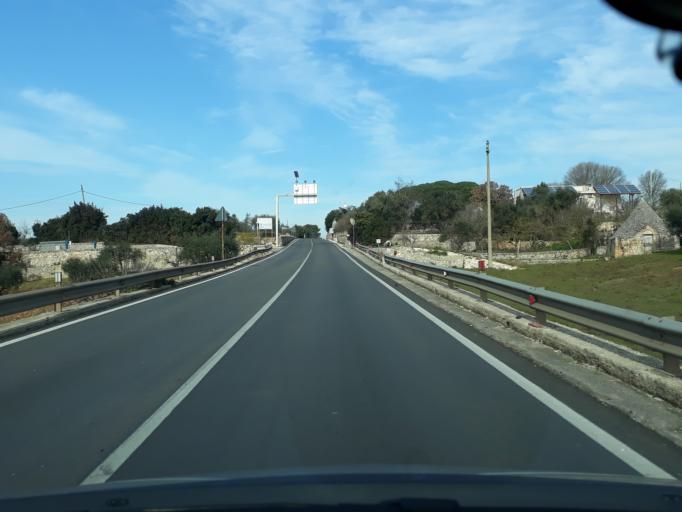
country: IT
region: Apulia
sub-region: Provincia di Bari
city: Locorotondo
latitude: 40.7660
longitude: 17.3328
